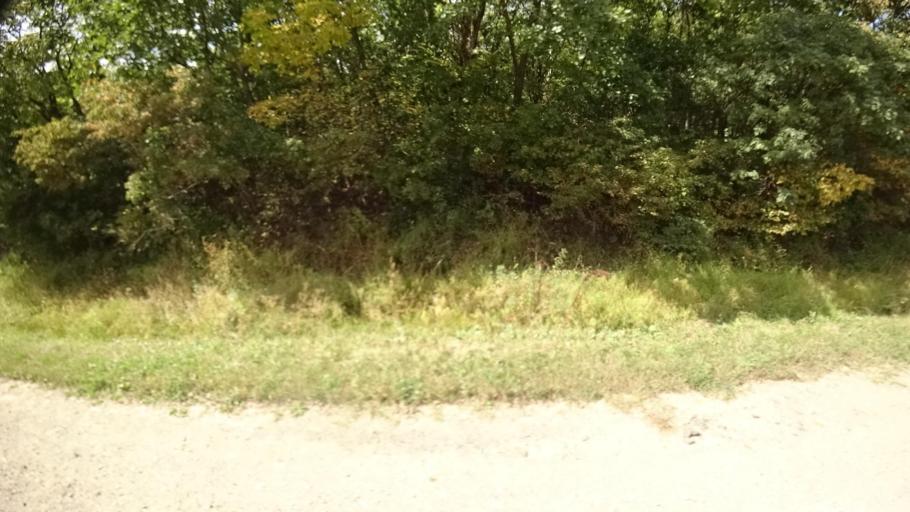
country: RU
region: Primorskiy
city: Yakovlevka
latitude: 44.6532
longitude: 133.5972
